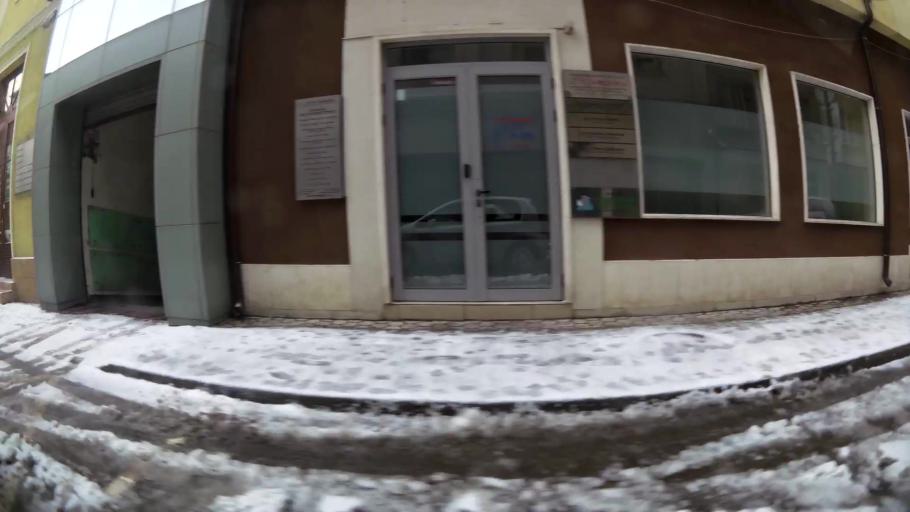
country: BG
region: Sofia-Capital
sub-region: Stolichna Obshtina
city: Sofia
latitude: 42.7020
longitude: 23.3219
